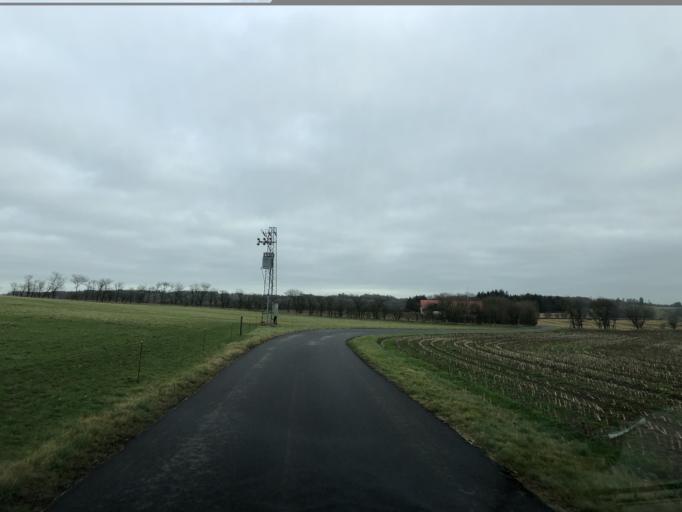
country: DK
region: Central Jutland
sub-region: Viborg Kommune
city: Stoholm
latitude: 56.4505
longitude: 9.1207
